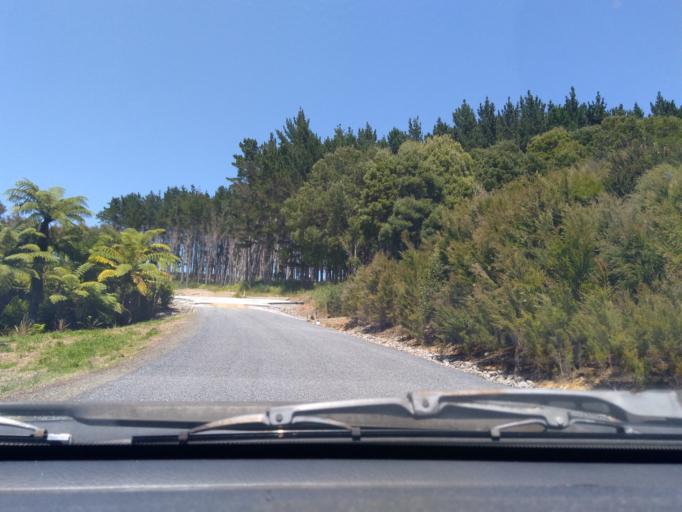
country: NZ
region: Northland
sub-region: Far North District
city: Taipa
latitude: -34.9977
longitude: 173.5111
